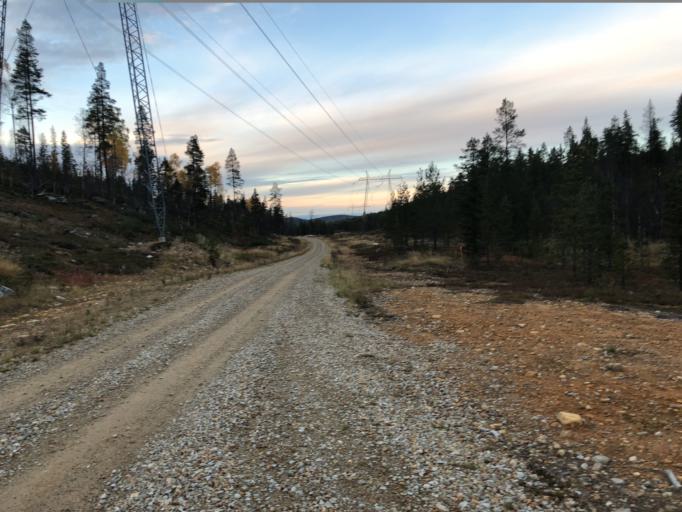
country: FI
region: Lapland
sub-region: Pohjois-Lappi
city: Ivalo
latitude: 68.5643
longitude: 27.6379
